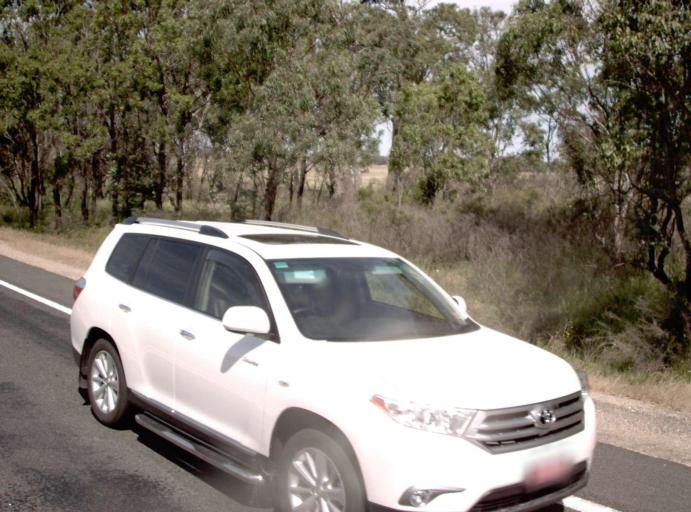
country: AU
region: Victoria
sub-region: East Gippsland
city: Bairnsdale
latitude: -37.8651
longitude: 147.4950
